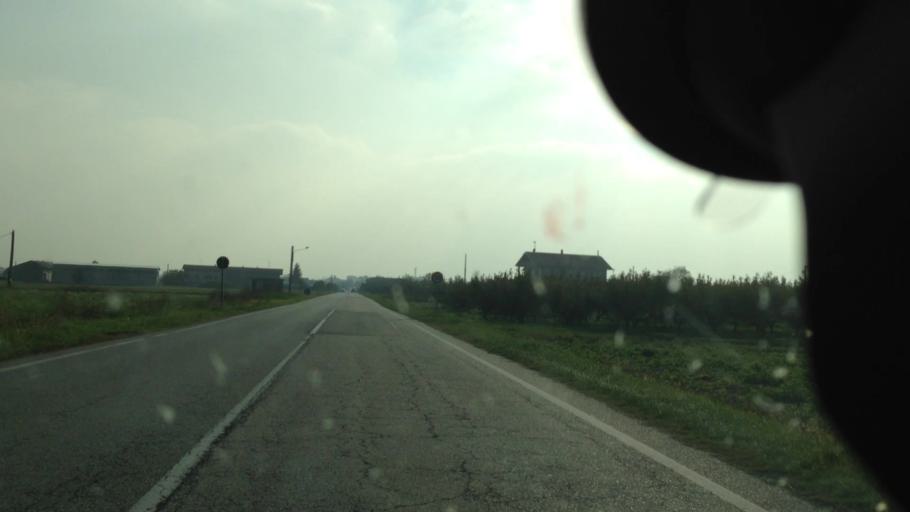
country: IT
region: Piedmont
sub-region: Provincia di Vercelli
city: Cigliano
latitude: 45.3283
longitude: 8.0374
